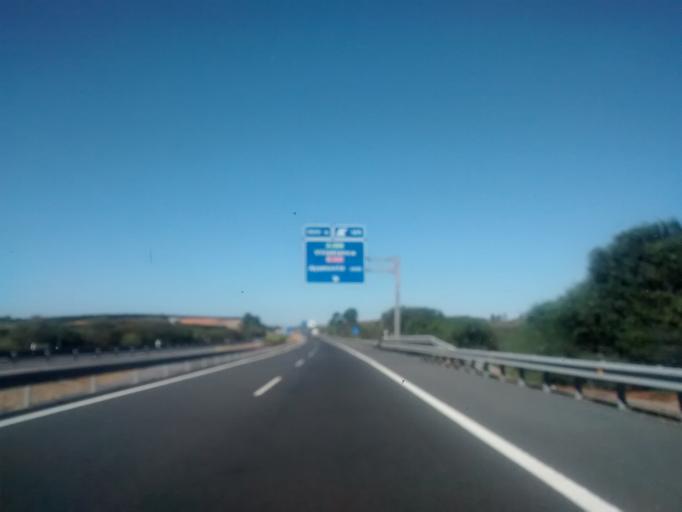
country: ES
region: Andalusia
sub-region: Provincia de Huelva
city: Villablanca
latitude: 37.2558
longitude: -7.3279
